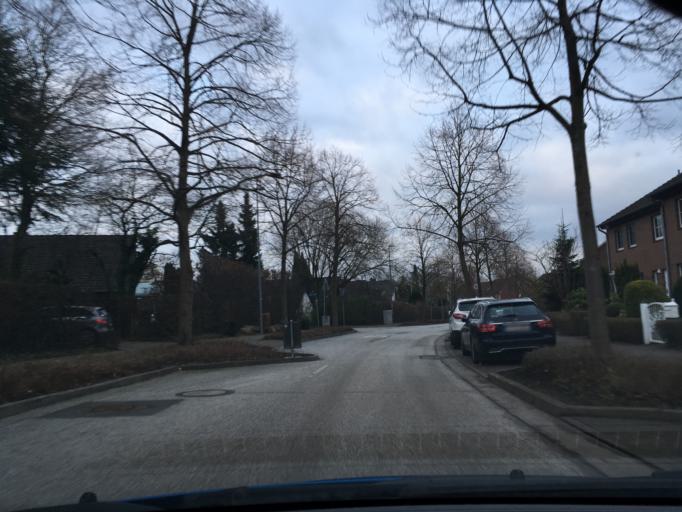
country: DE
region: Schleswig-Holstein
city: Wedel
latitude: 53.5893
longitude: 9.6942
